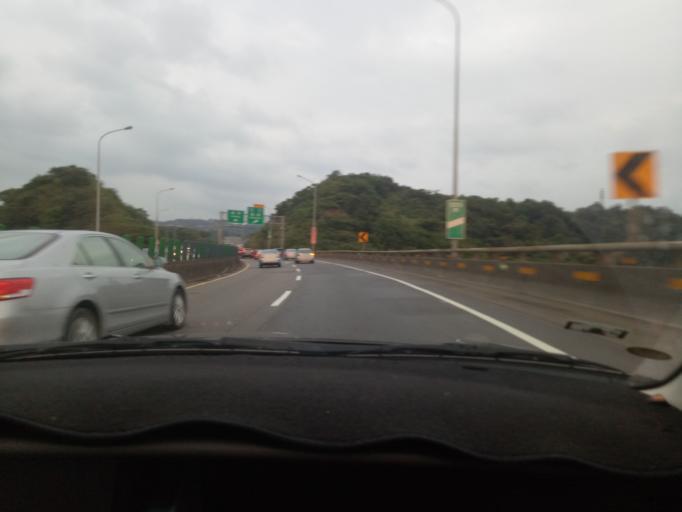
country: TW
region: Taiwan
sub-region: Keelung
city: Keelung
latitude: 25.1047
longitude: 121.7289
